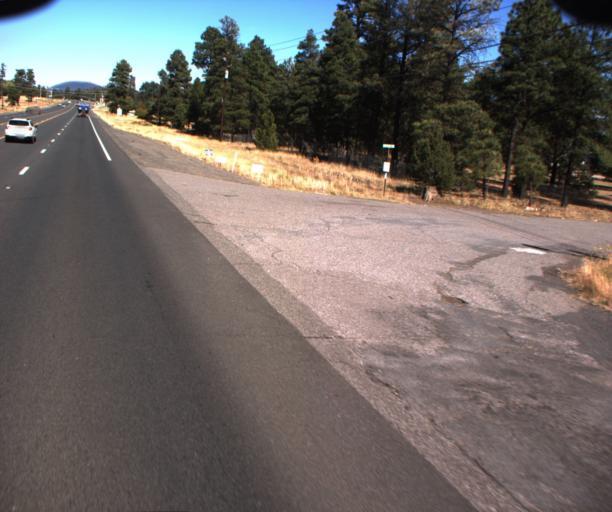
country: US
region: Arizona
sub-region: Coconino County
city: Flagstaff
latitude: 35.2654
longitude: -111.5473
